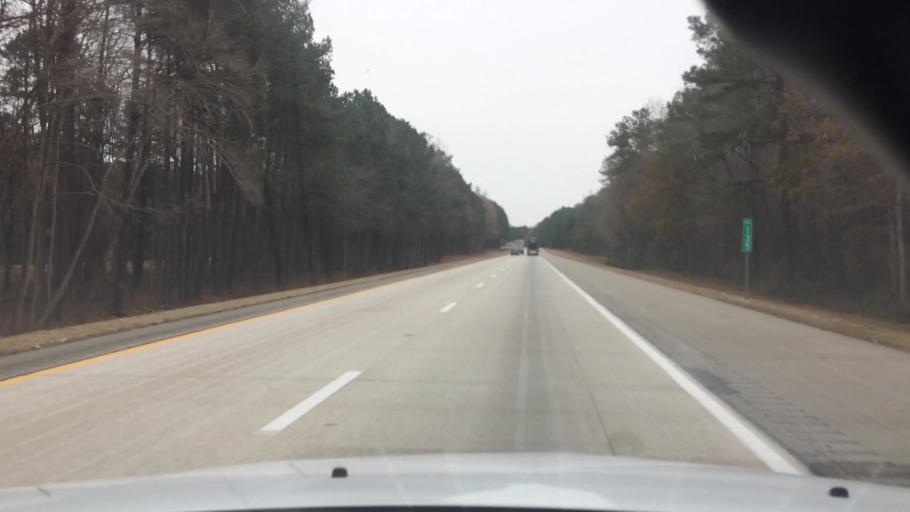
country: US
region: North Carolina
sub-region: Nash County
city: Nashville
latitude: 35.9374
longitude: -77.8978
